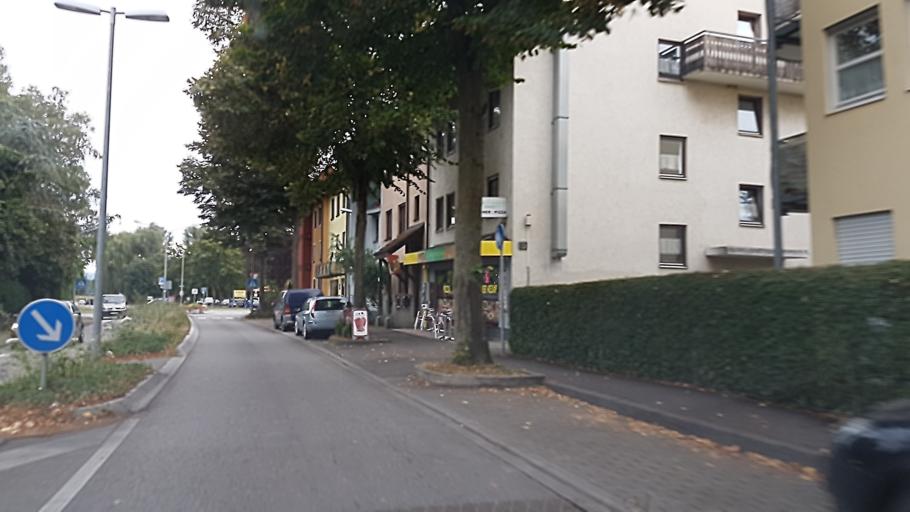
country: DE
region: Baden-Wuerttemberg
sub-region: Freiburg Region
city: Merdingen
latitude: 47.9999
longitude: 7.7178
